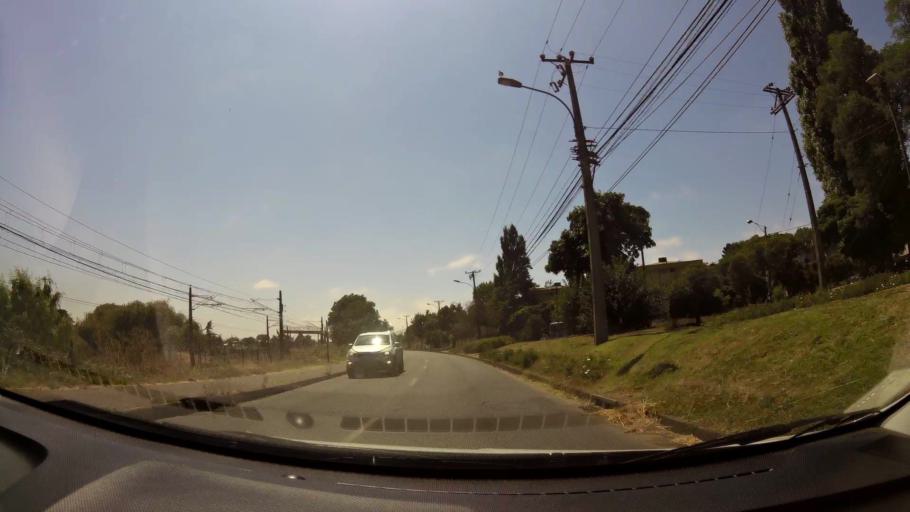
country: CL
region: Biobio
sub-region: Provincia de Concepcion
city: Concepcion
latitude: -36.8124
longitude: -73.0664
